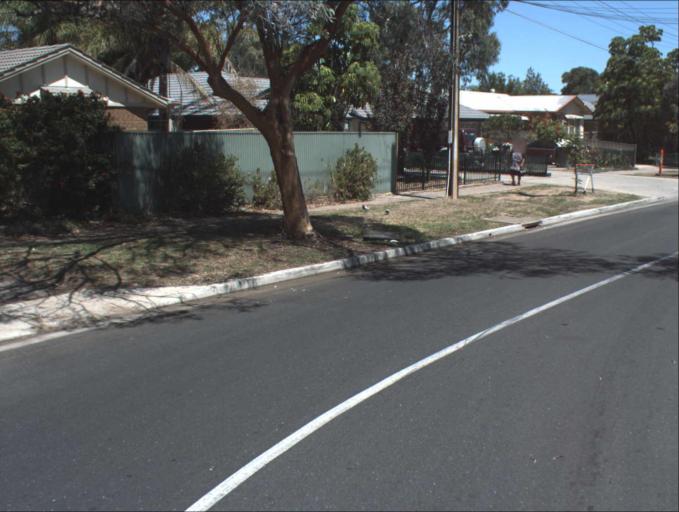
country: AU
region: South Australia
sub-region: Port Adelaide Enfield
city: Klemzig
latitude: -34.8694
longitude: 138.6306
